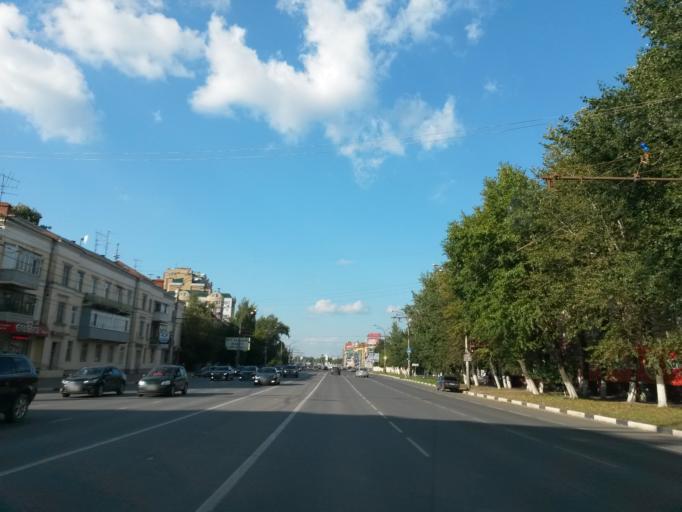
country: RU
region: Ivanovo
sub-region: Gorod Ivanovo
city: Ivanovo
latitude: 56.9784
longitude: 40.9774
